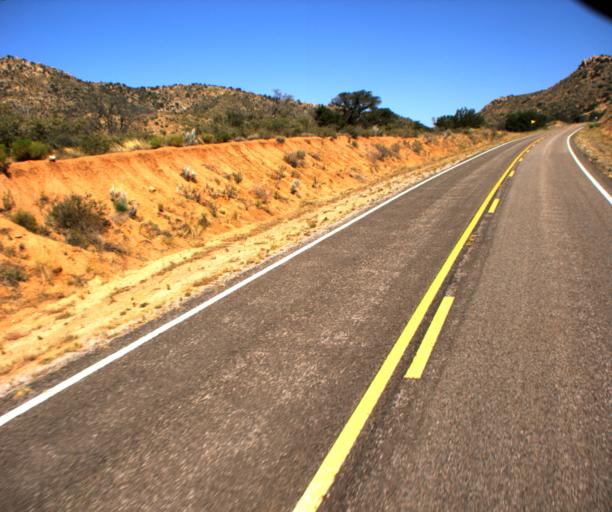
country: US
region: Arizona
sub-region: Graham County
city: Swift Trail Junction
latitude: 32.5716
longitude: -109.8304
